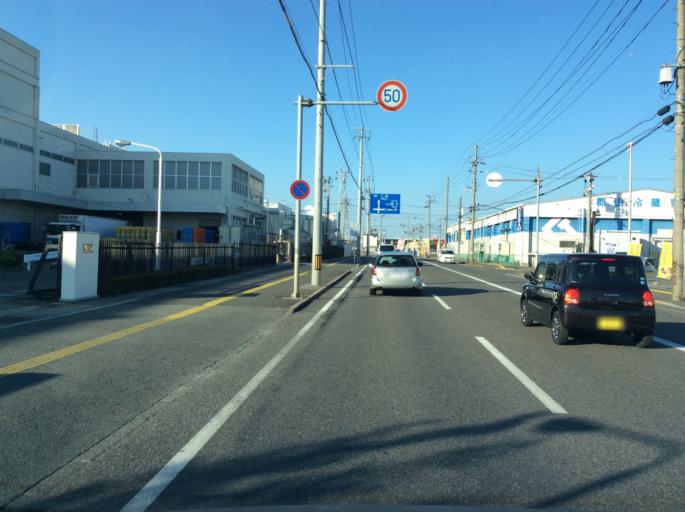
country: JP
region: Fukushima
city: Koriyama
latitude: 37.4079
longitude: 140.3968
